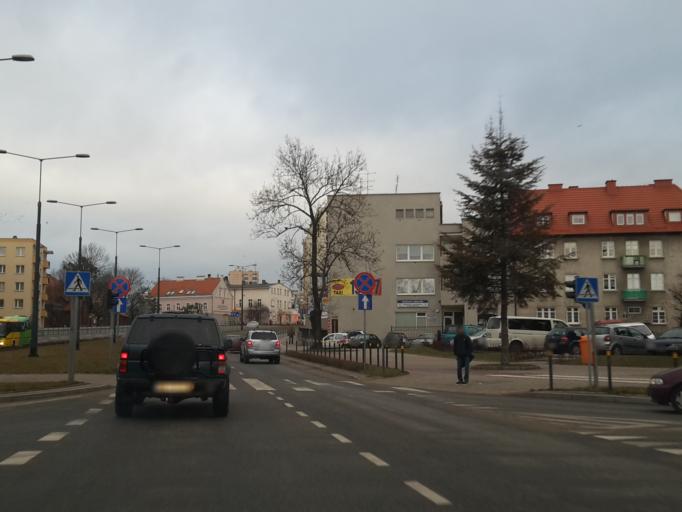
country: PL
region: Warmian-Masurian Voivodeship
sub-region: Powiat elblaski
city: Elblag
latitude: 54.1611
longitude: 19.4045
